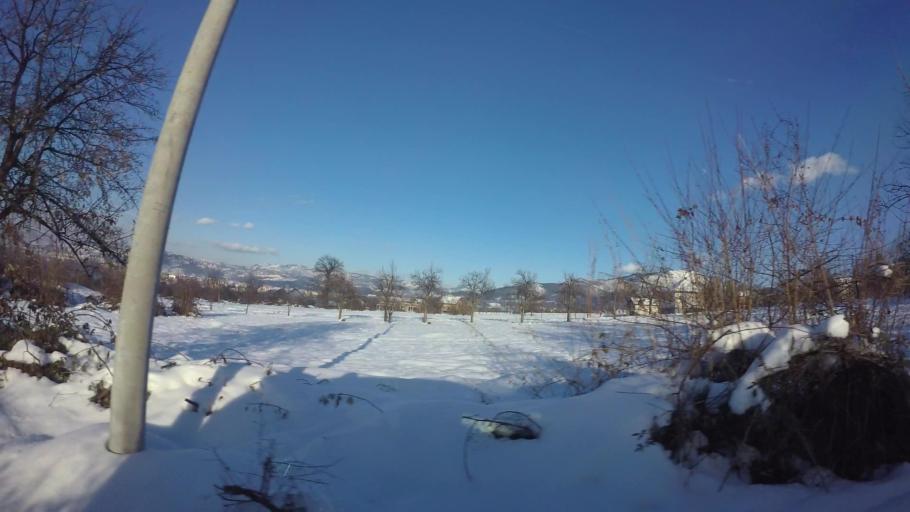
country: BA
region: Federation of Bosnia and Herzegovina
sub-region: Kanton Sarajevo
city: Sarajevo
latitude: 43.8091
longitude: 18.3507
